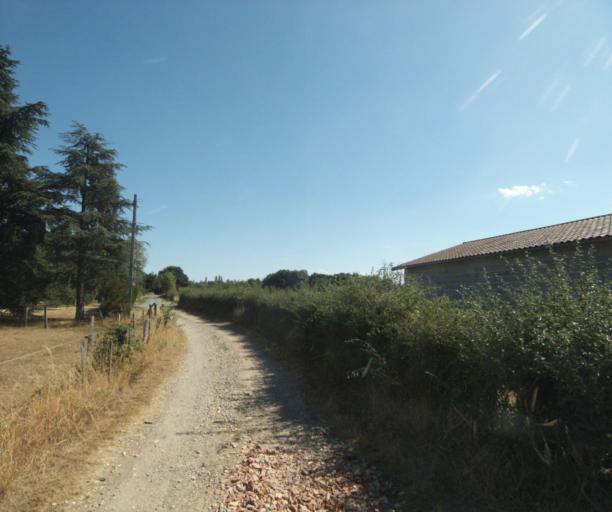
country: FR
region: Rhone-Alpes
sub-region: Departement du Rhone
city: Lozanne
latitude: 45.8416
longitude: 4.7032
